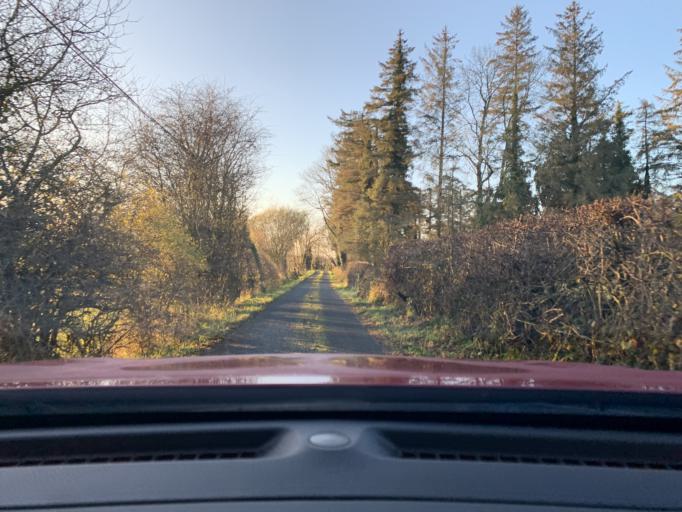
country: IE
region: Connaught
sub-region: Sligo
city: Ballymote
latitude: 54.0801
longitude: -8.5465
